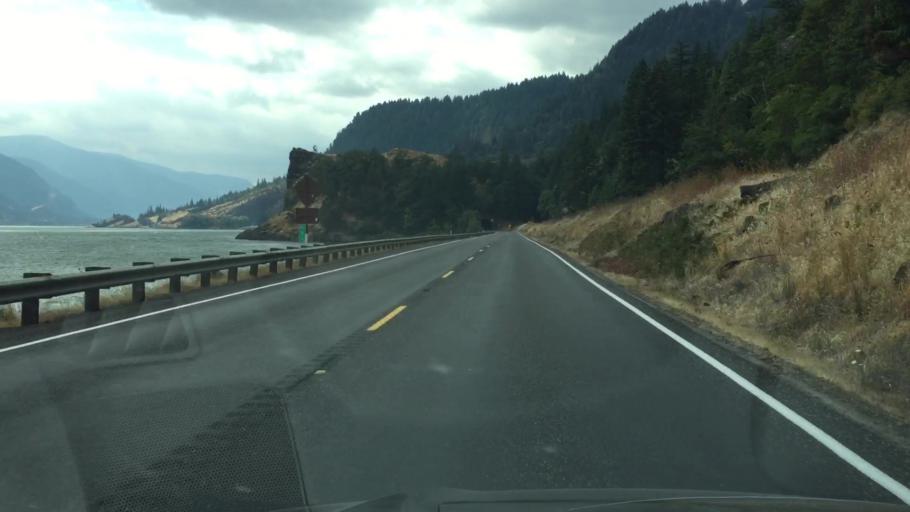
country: US
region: Oregon
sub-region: Hood River County
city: Hood River
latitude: 45.7203
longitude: -121.5907
